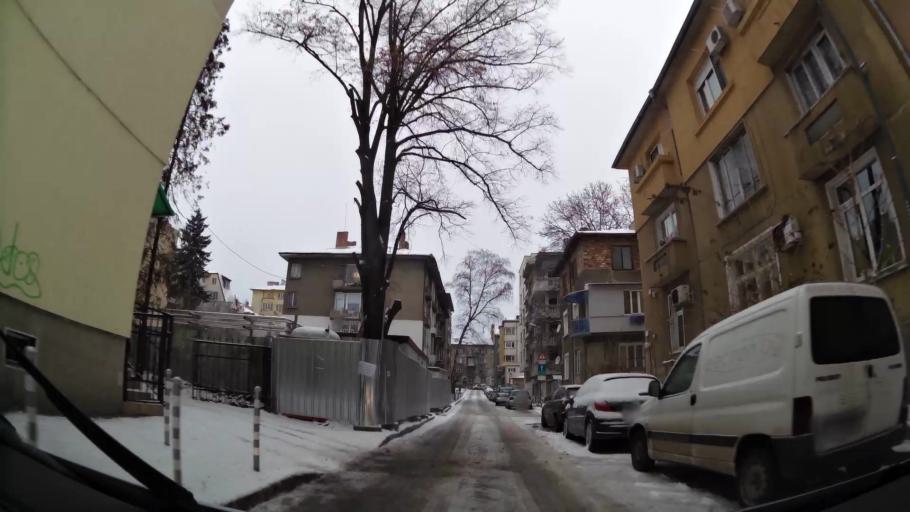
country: BG
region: Sofia-Capital
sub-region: Stolichna Obshtina
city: Sofia
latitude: 42.7001
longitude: 23.3360
